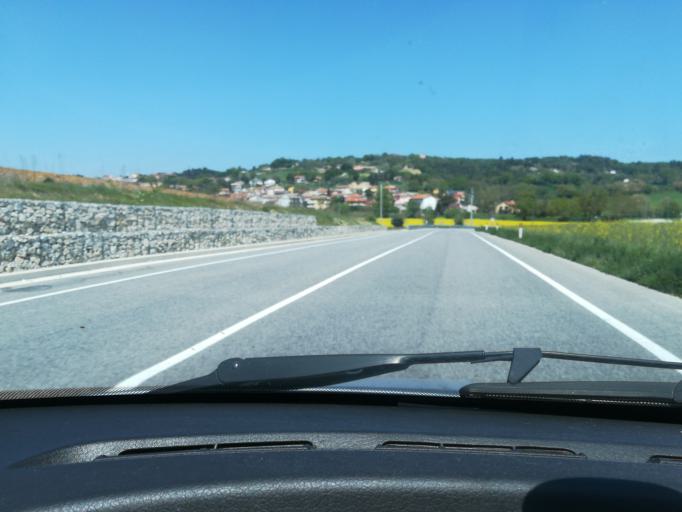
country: IT
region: The Marches
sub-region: Provincia di Ancona
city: Villa Musone
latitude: 43.4560
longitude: 13.5812
